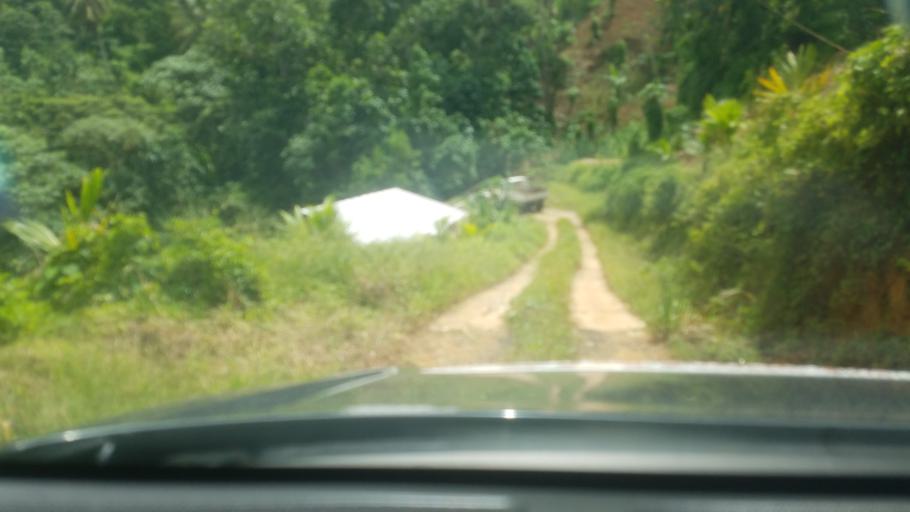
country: LC
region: Micoud Quarter
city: Micoud
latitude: 13.8042
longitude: -60.9507
